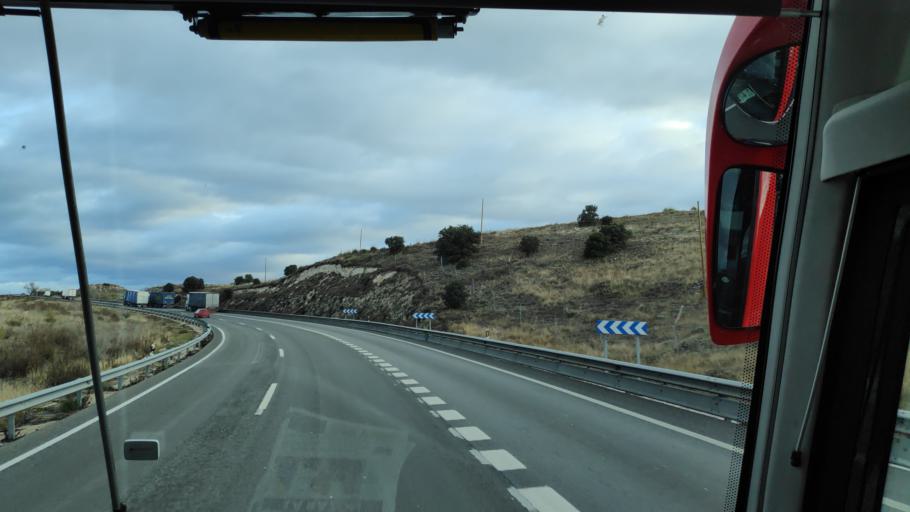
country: ES
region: Madrid
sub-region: Provincia de Madrid
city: Tielmes
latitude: 40.1997
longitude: -3.3142
